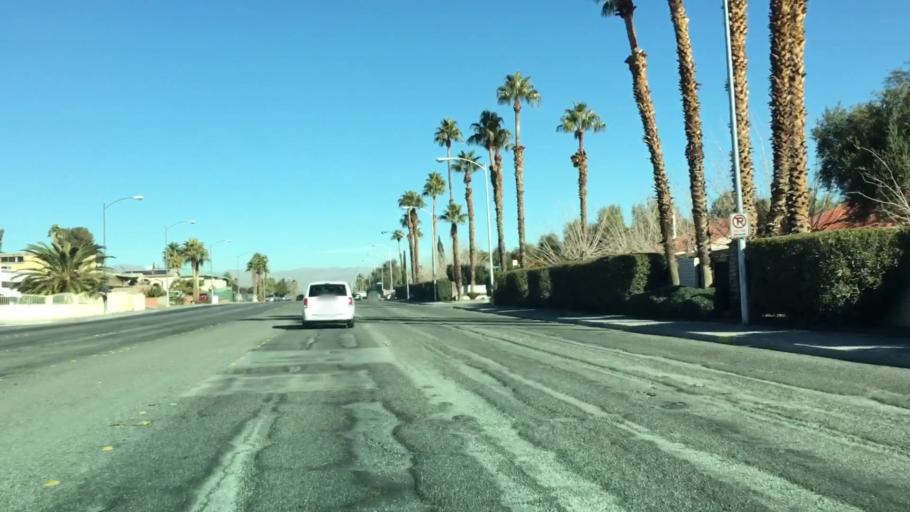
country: US
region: Nevada
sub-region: Clark County
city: Winchester
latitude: 36.1245
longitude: -115.1187
